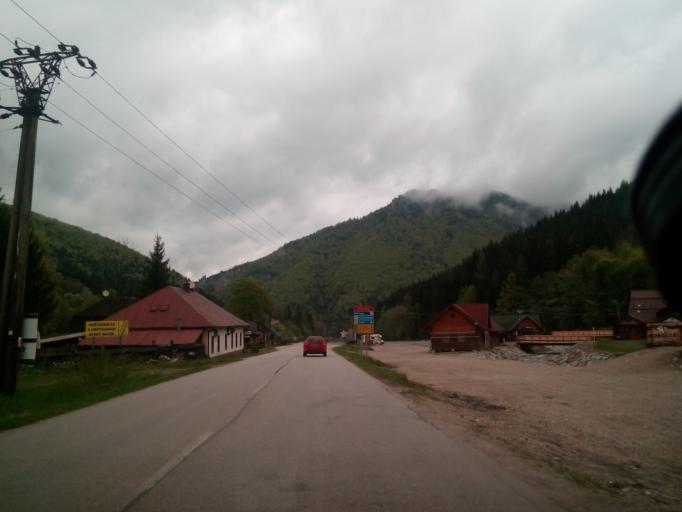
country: SK
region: Zilinsky
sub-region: Okres Zilina
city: Terchova
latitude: 49.2279
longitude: 19.0347
